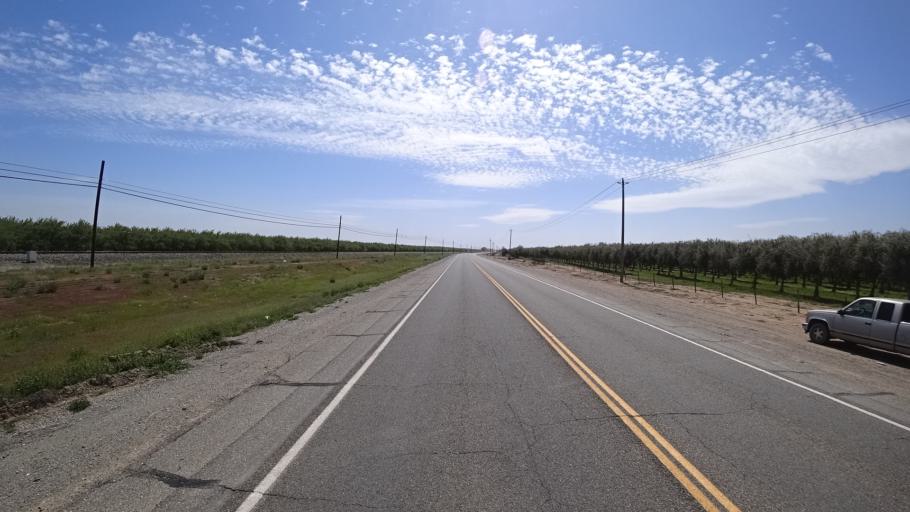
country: US
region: California
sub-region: Glenn County
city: Willows
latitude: 39.5816
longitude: -122.1941
